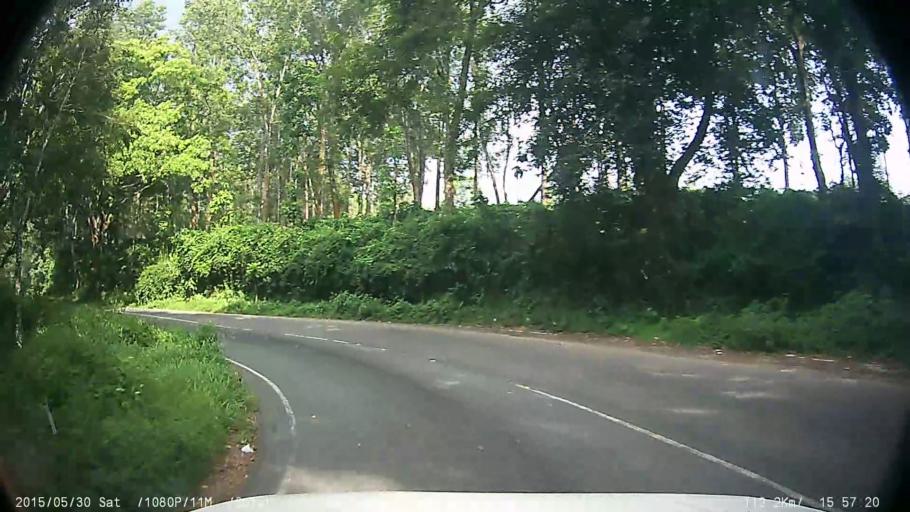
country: IN
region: Kerala
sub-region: Wayanad
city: Kalpetta
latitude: 11.6549
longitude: 76.0865
